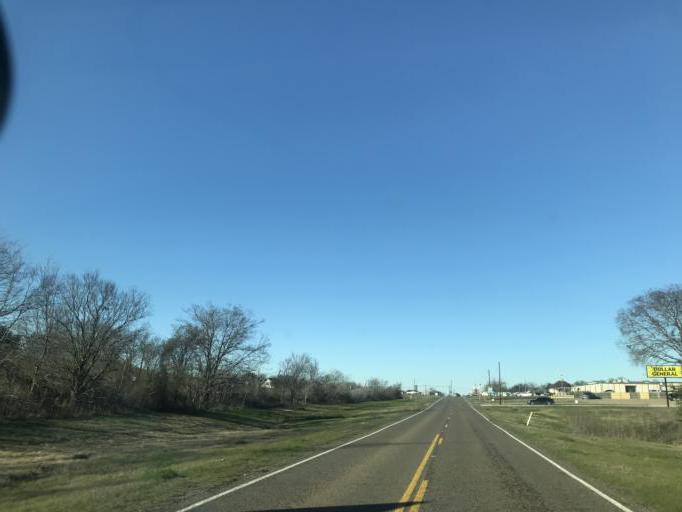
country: US
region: Texas
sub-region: Ellis County
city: Ferris
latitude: 32.5269
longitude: -96.6645
